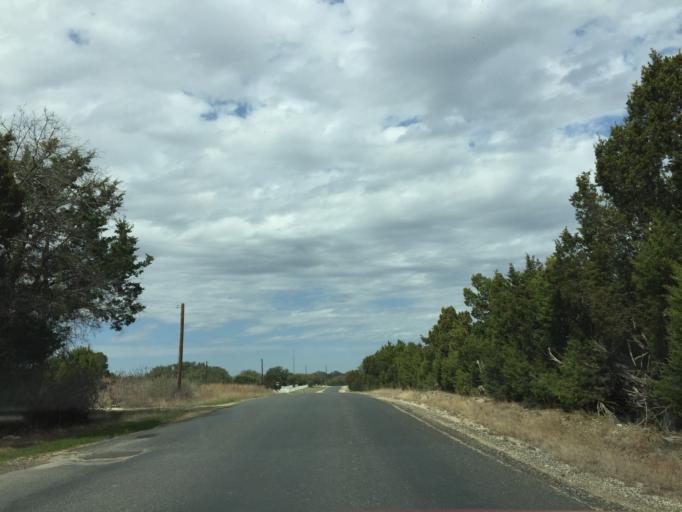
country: US
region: Texas
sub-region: Burnet County
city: Bertram
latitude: 30.7277
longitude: -97.9336
